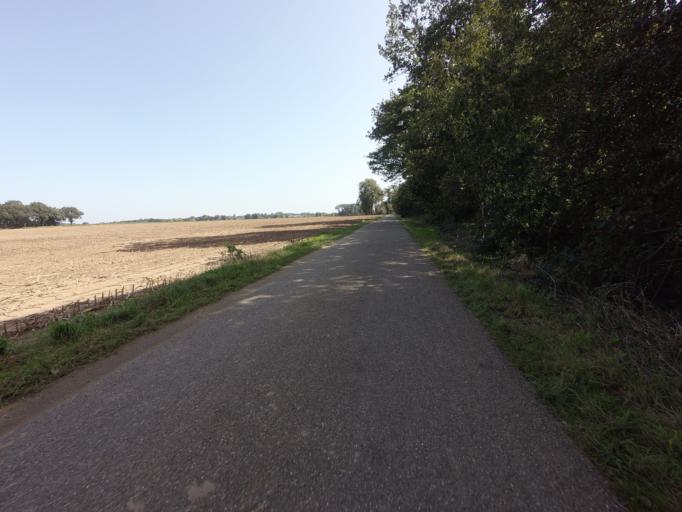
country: NL
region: Limburg
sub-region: Gemeente Roerdalen
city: Sint Odilienberg
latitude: 51.1554
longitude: 5.9884
